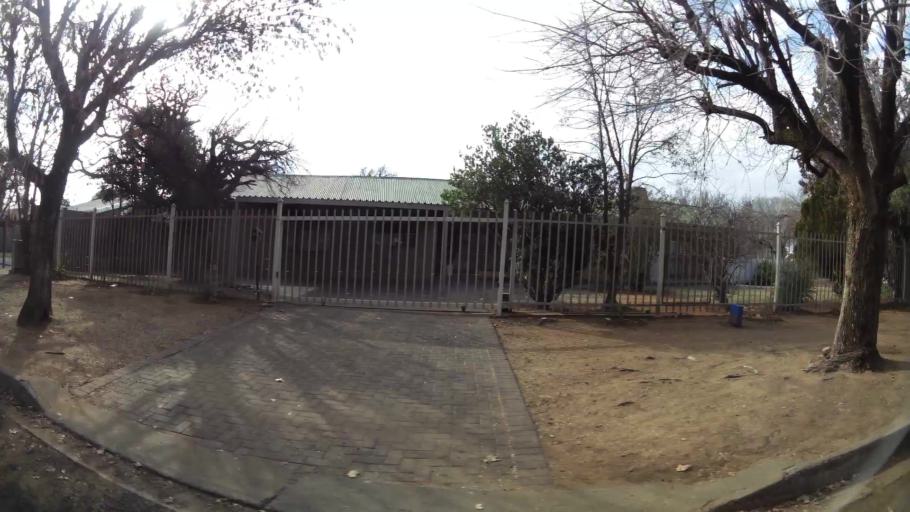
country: ZA
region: Orange Free State
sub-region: Mangaung Metropolitan Municipality
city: Bloemfontein
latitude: -29.0856
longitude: 26.2382
